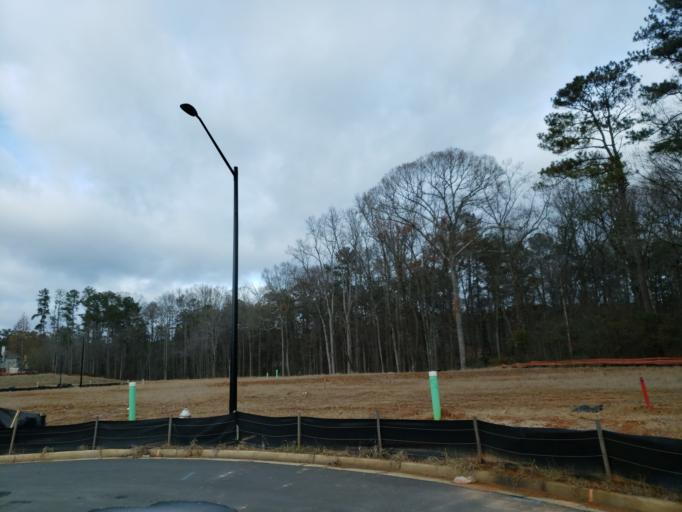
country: US
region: Georgia
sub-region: Cobb County
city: Fair Oaks
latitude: 33.8914
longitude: -84.6069
